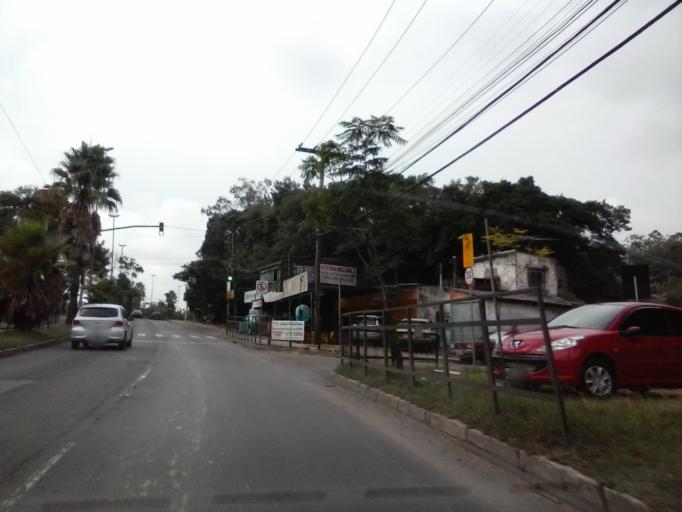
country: BR
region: Rio Grande do Sul
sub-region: Porto Alegre
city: Porto Alegre
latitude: -30.0618
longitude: -51.1489
